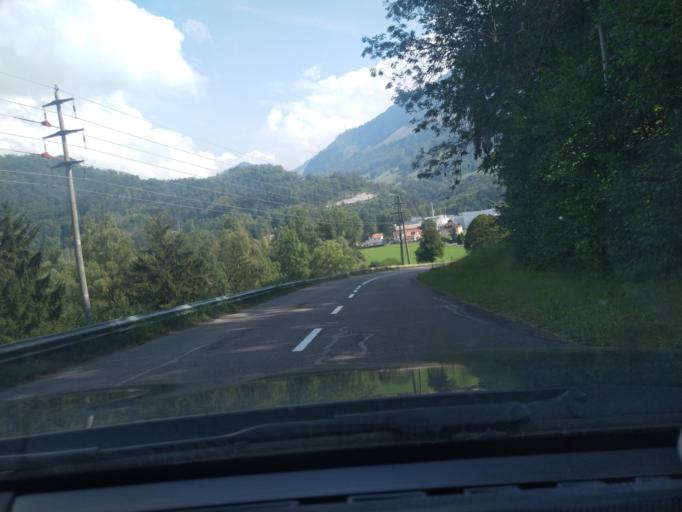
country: CH
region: Fribourg
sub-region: Gruyere District
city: Broc
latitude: 46.6108
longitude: 7.0994
